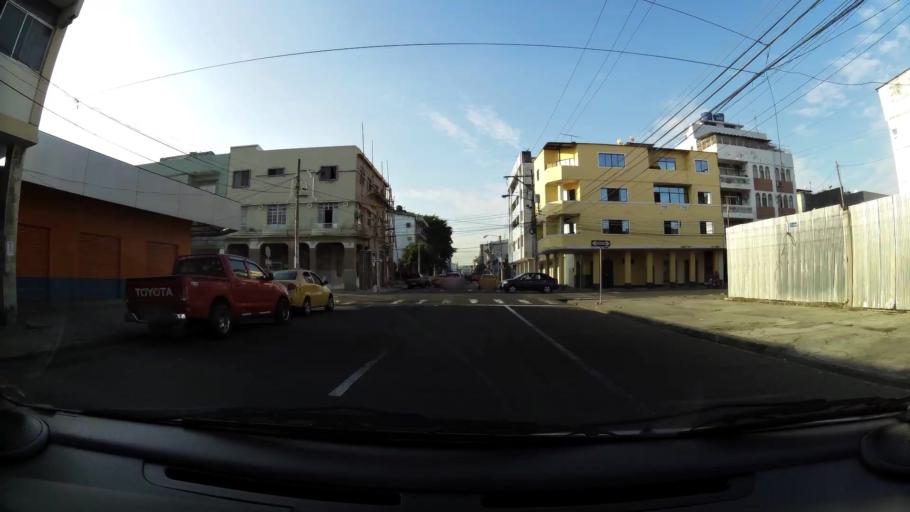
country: EC
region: Guayas
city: Guayaquil
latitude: -2.2120
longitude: -79.8881
